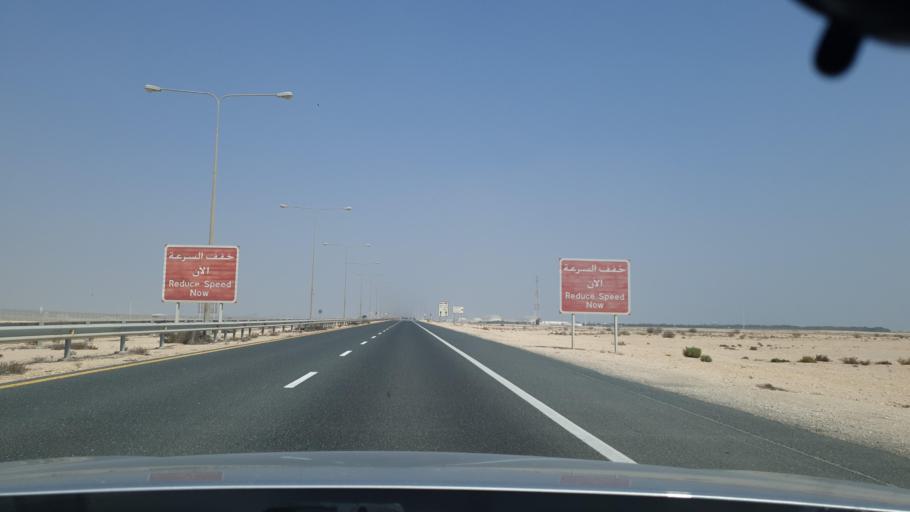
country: QA
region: Al Khawr
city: Al Khawr
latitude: 25.8323
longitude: 51.5243
